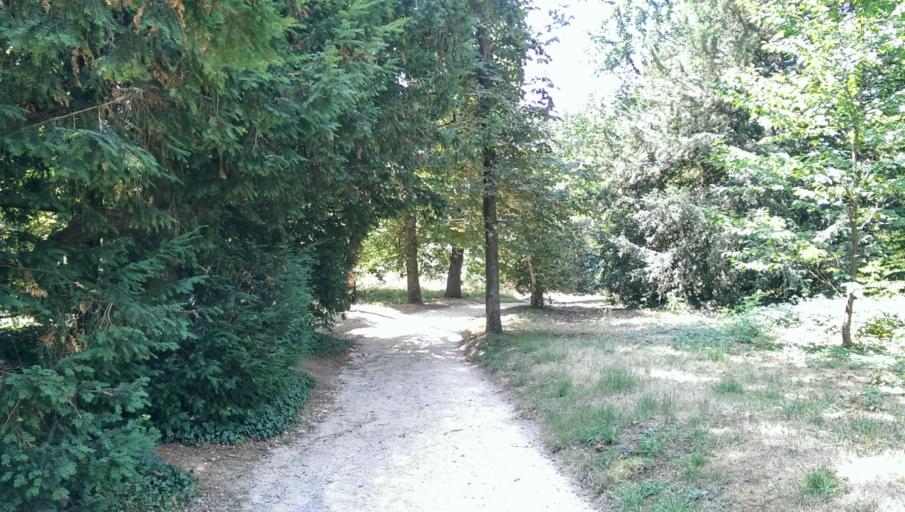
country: FR
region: Pays de la Loire
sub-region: Departement de la Loire-Atlantique
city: Clisson
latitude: 47.0844
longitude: -1.2736
